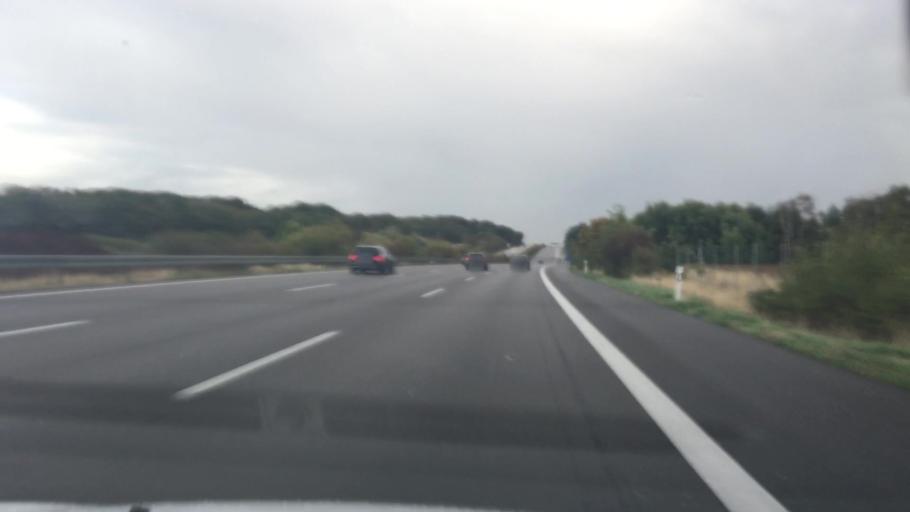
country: DE
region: Lower Saxony
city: Konigslutter am Elm
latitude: 52.3083
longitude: 10.8339
